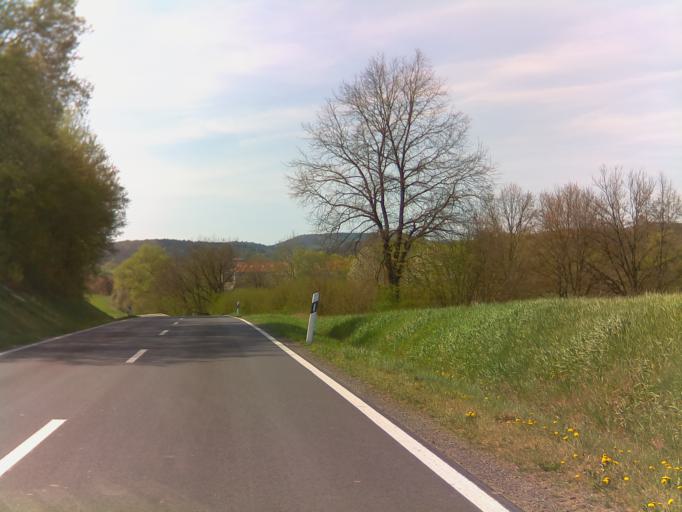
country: DE
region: Bavaria
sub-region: Regierungsbezirk Unterfranken
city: Burgpreppach
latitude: 50.1572
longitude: 10.6032
